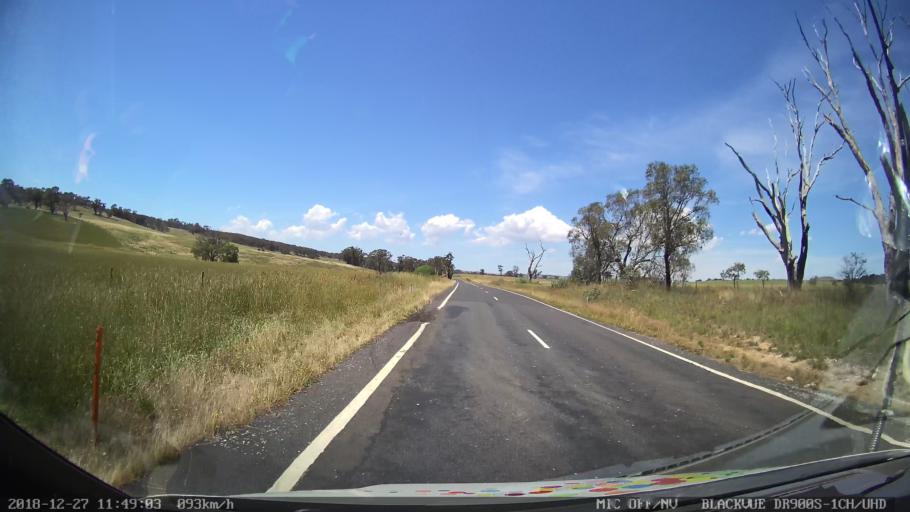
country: AU
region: New South Wales
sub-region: Bathurst Regional
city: Perthville
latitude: -33.6134
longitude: 149.4352
